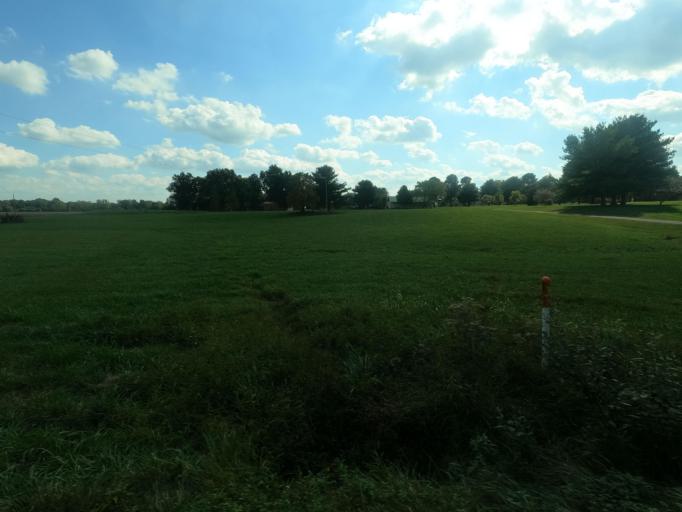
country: US
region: Illinois
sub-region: Massac County
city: Metropolis
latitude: 37.1913
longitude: -88.7168
